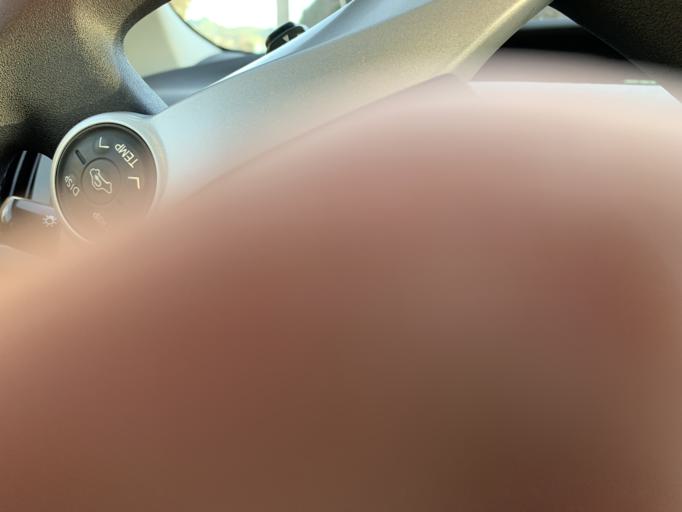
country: US
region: California
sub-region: Contra Costa County
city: North Richmond
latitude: 37.9349
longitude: -122.4093
